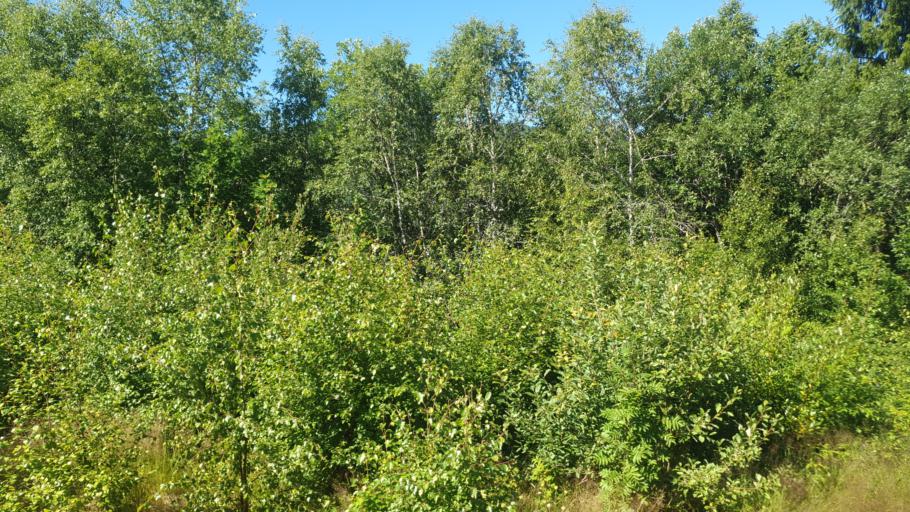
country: NO
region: Sor-Trondelag
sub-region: Meldal
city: Meldal
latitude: 63.1697
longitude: 9.7484
